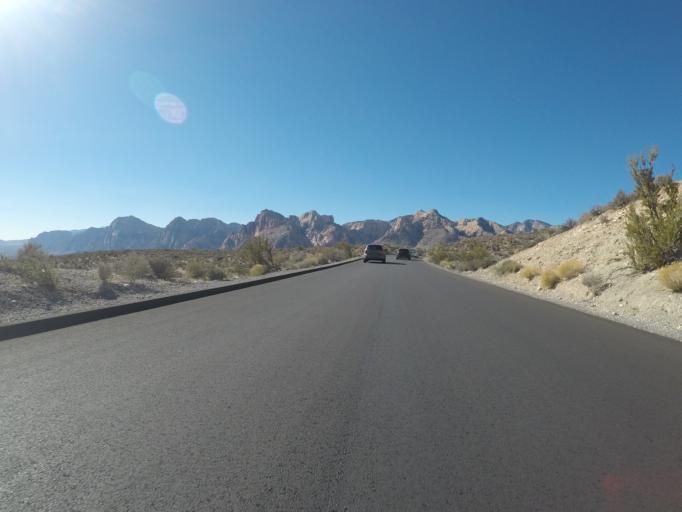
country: US
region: Nevada
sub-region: Clark County
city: Summerlin South
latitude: 36.1721
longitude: -115.4640
